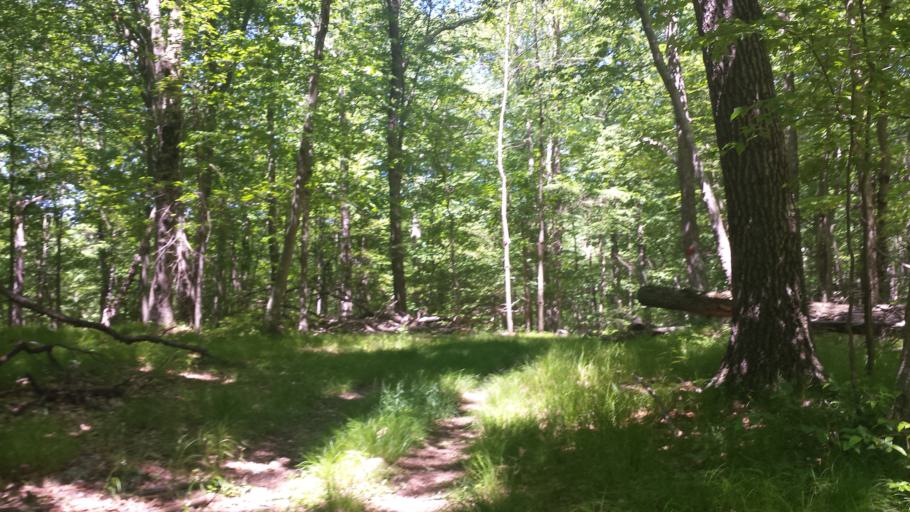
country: US
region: New York
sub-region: Westchester County
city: Pound Ridge
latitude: 41.2367
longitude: -73.5806
